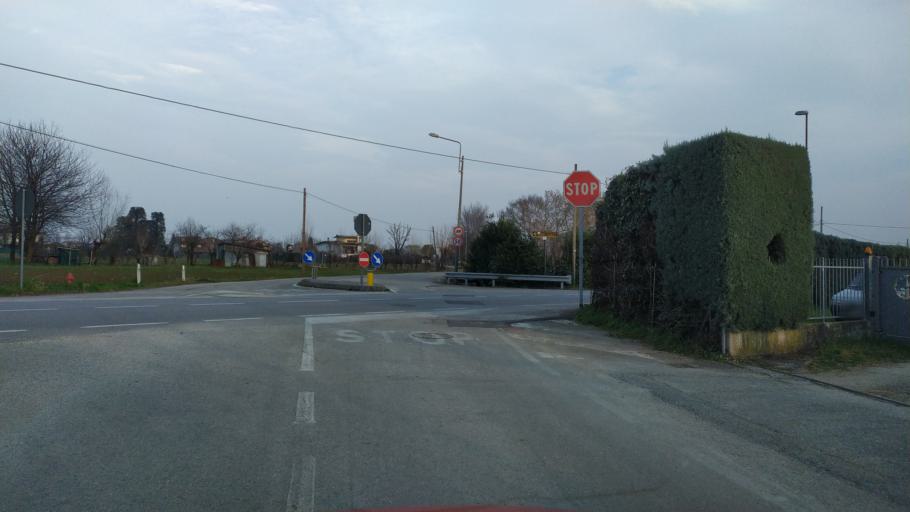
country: IT
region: Veneto
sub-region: Provincia di Vicenza
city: Marano Vicentino
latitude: 45.6875
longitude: 11.4465
